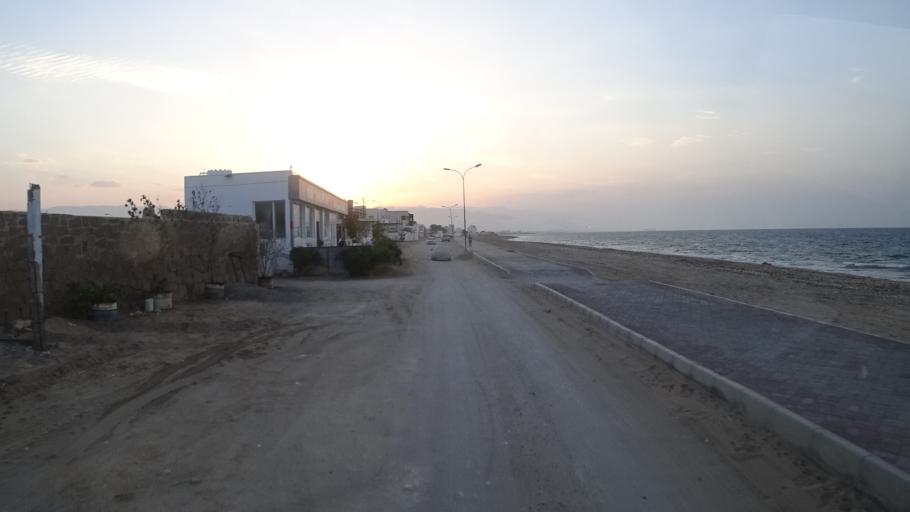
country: OM
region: Ash Sharqiyah
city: Sur
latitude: 22.5920
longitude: 59.5017
